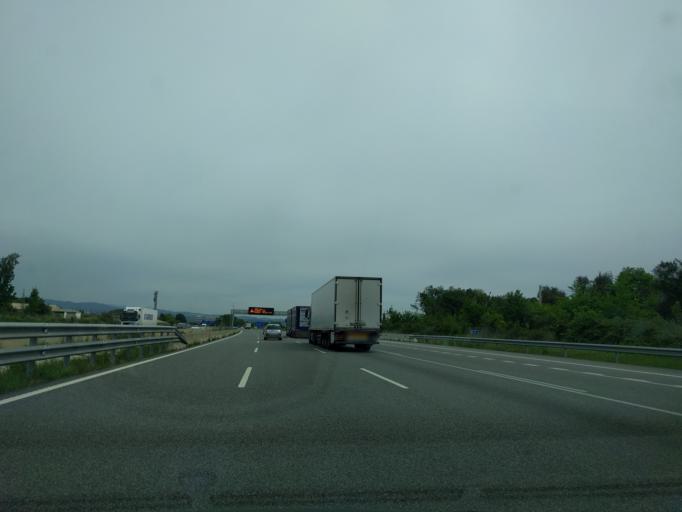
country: ES
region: Catalonia
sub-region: Provincia de Girona
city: Fornells de la Selva
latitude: 41.9391
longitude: 2.7884
